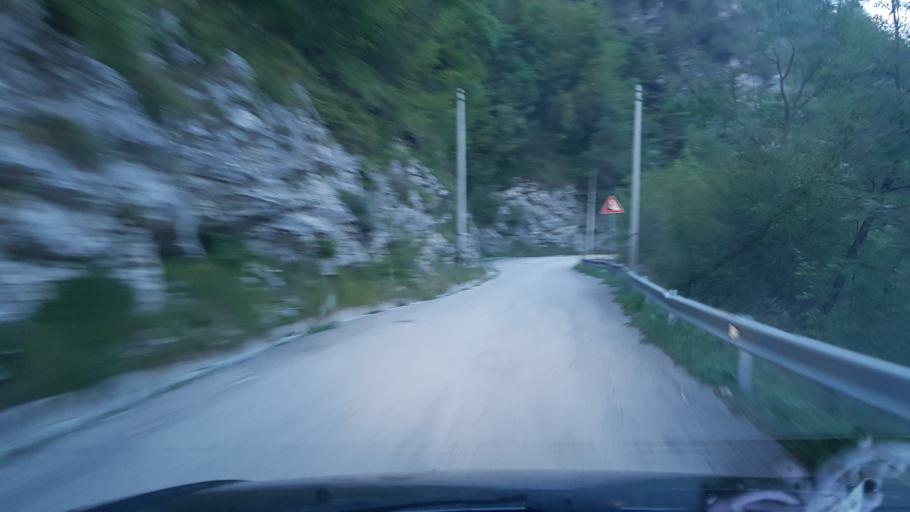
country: IT
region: Friuli Venezia Giulia
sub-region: Provincia di Pordenone
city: Frisanco
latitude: 46.2562
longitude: 12.7112
